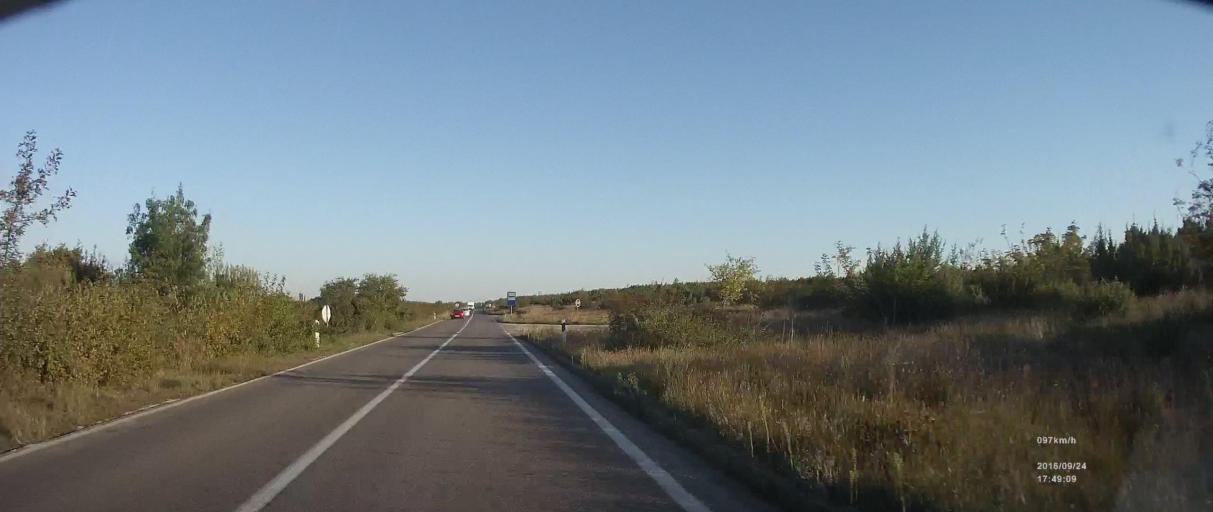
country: HR
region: Zadarska
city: Polaca
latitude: 44.0569
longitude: 15.5462
